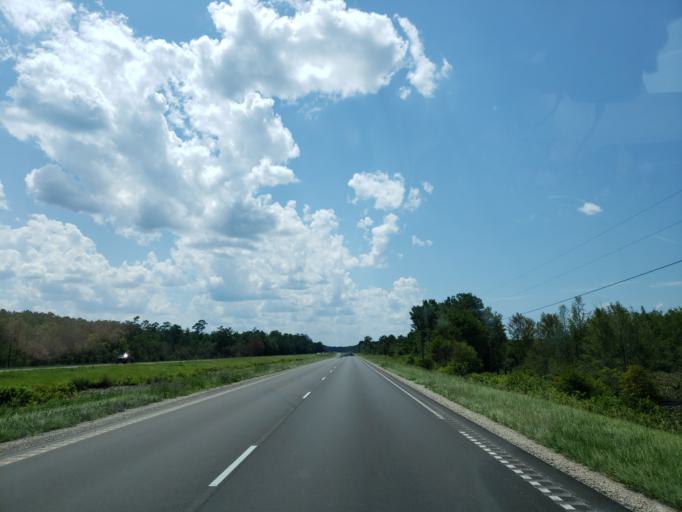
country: US
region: Mississippi
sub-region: Perry County
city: New Augusta
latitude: 31.2094
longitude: -89.1011
